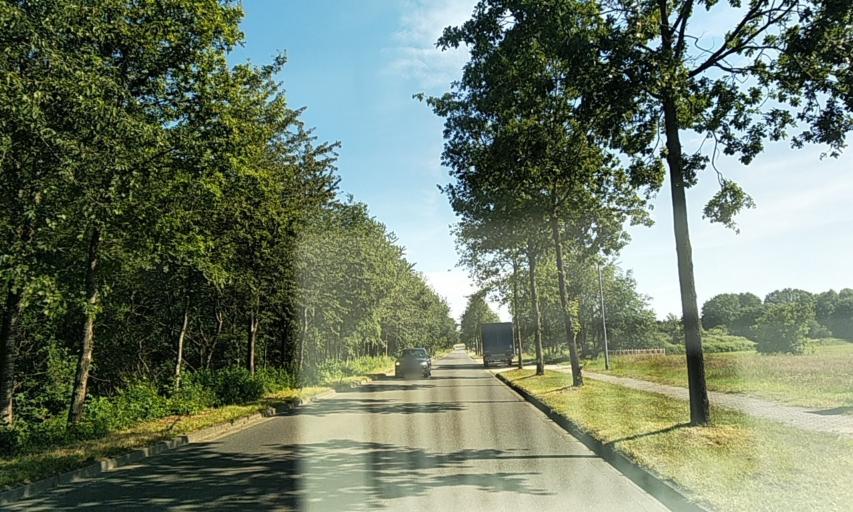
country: DE
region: Schleswig-Holstein
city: Fockbek
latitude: 54.3250
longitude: 9.6164
